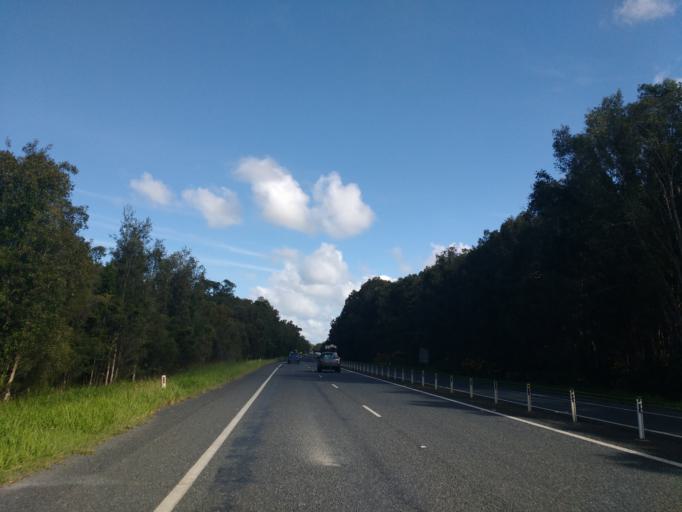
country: AU
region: New South Wales
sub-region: Ballina
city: Ballina
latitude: -28.9095
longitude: 153.4788
